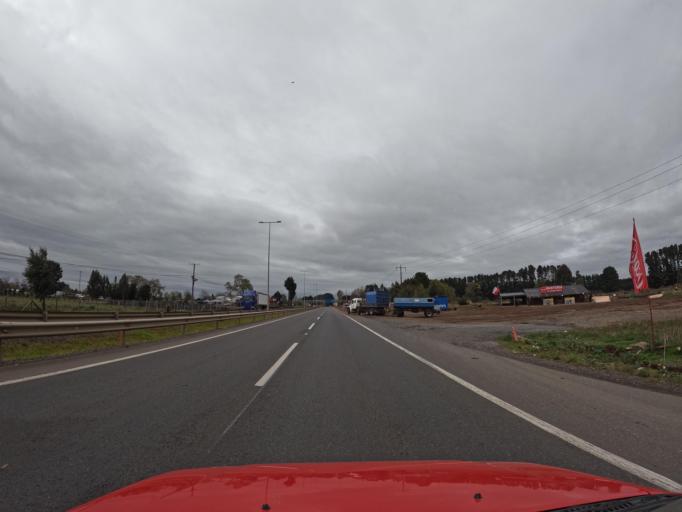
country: CL
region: Araucania
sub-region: Provincia de Malleco
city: Victoria
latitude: -38.1290
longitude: -72.3249
